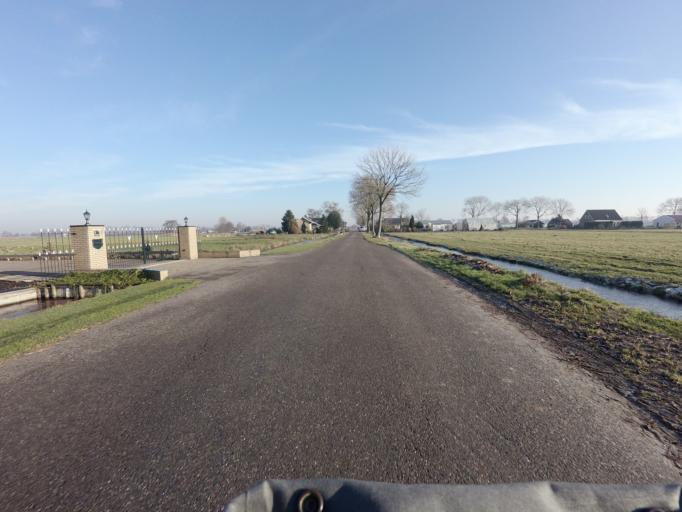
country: NL
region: Utrecht
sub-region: Gemeente De Ronde Venen
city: Mijdrecht
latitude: 52.1720
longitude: 4.8532
